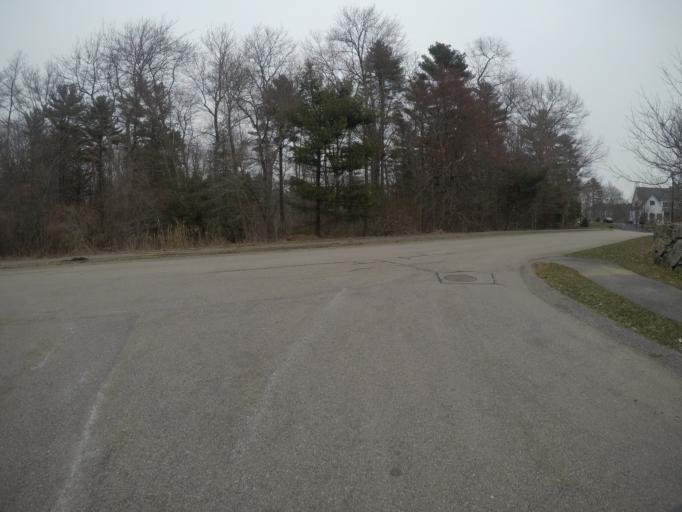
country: US
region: Massachusetts
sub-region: Bristol County
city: Easton
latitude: 42.0356
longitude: -71.1549
